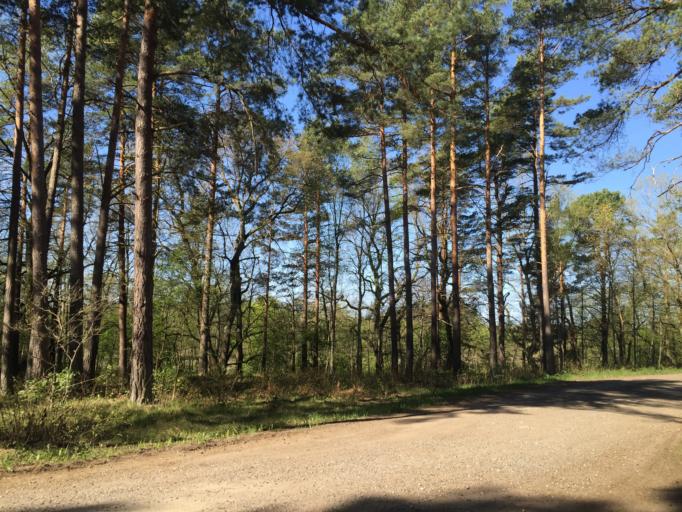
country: LV
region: Adazi
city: Adazi
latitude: 57.0907
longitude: 24.3403
